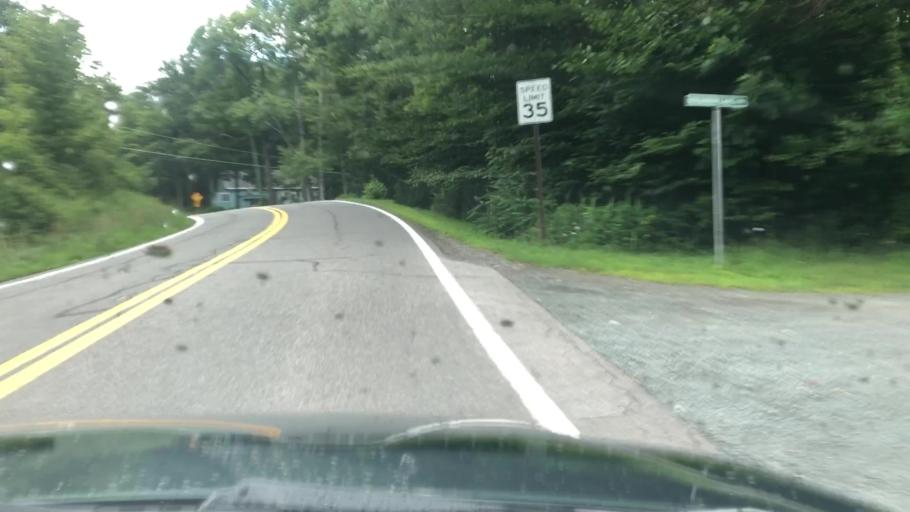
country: US
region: Pennsylvania
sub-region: Monroe County
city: Mountainhome
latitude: 41.2949
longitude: -75.2208
